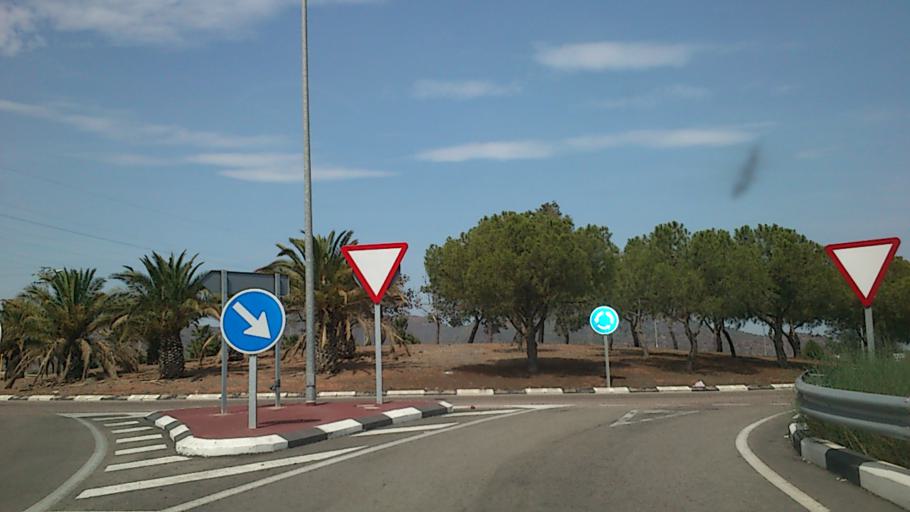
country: ES
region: Valencia
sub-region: Provincia de Valencia
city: Museros
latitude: 39.6080
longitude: -0.3438
